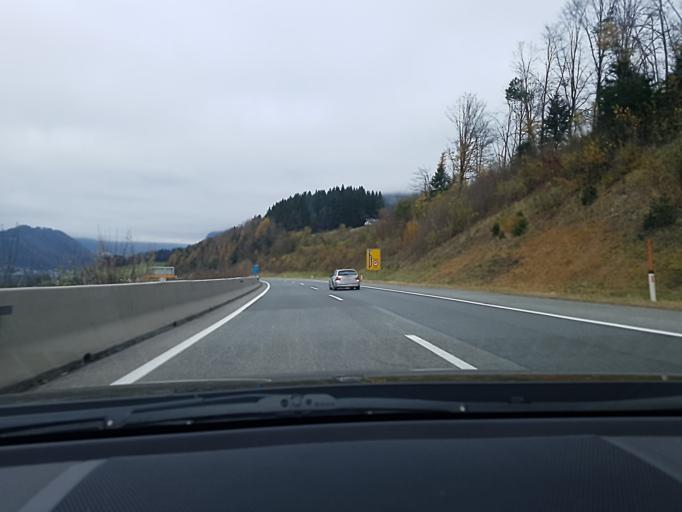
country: AT
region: Salzburg
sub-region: Politischer Bezirk Sankt Johann im Pongau
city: Pfarrwerfen
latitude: 47.4505
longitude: 13.2179
